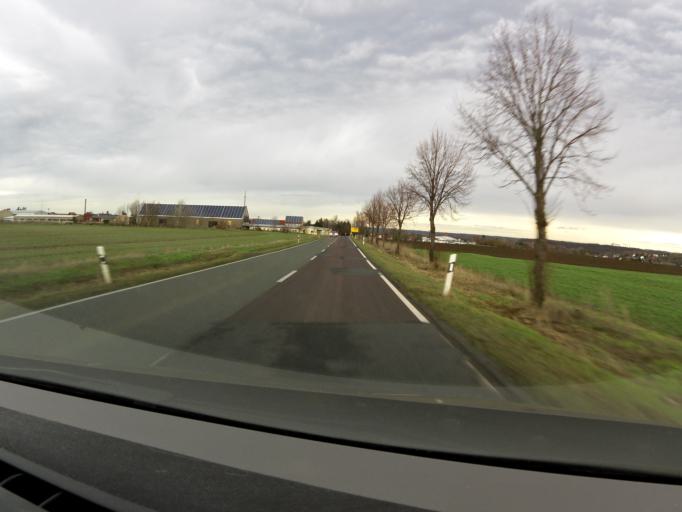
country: DE
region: Saxony-Anhalt
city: Alsleben
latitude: 51.6973
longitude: 11.6647
